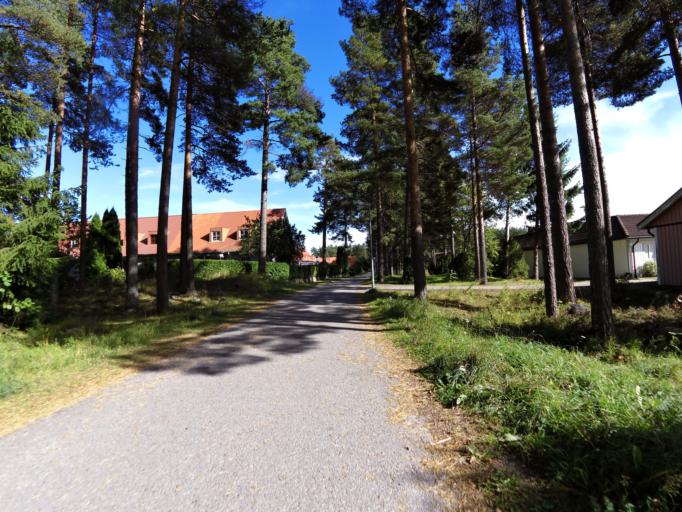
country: SE
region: Gaevleborg
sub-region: Gavle Kommun
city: Gavle
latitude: 60.6686
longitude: 17.2177
